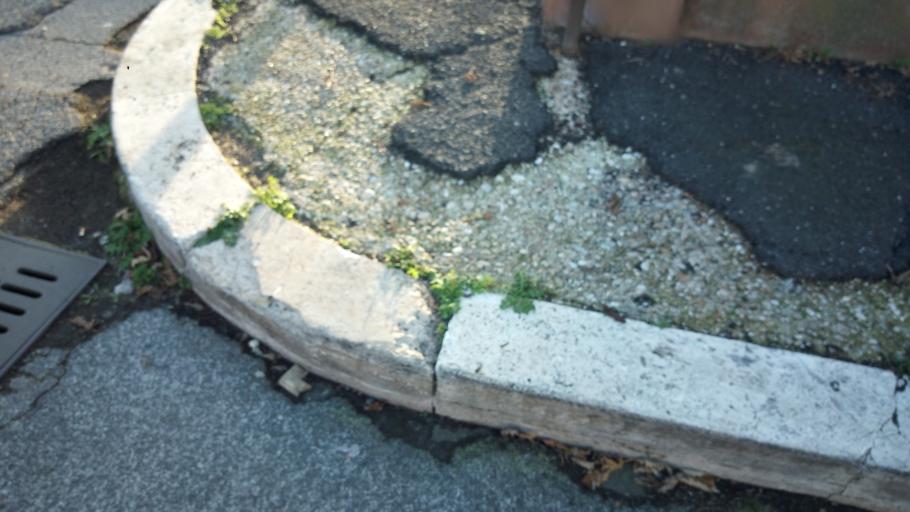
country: IT
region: Latium
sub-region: Citta metropolitana di Roma Capitale
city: Ciampino
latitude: 41.8043
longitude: 12.5951
